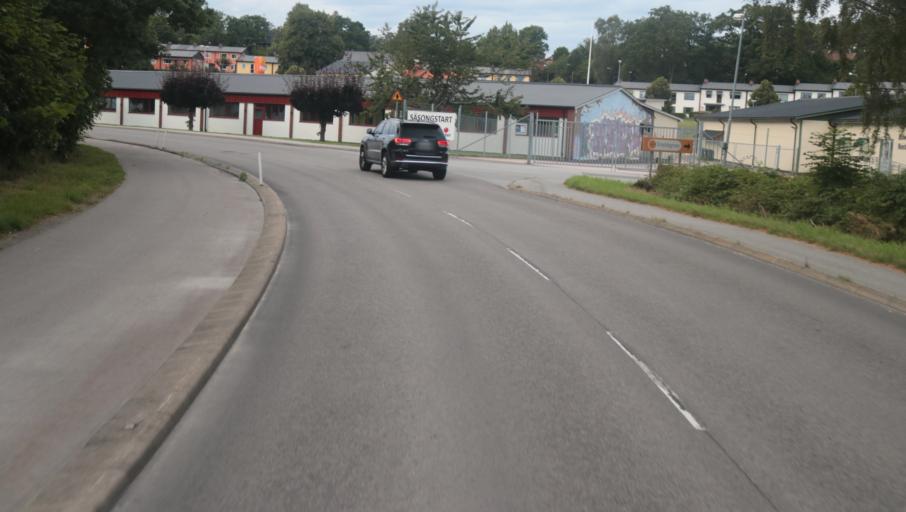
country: SE
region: Blekinge
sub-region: Karlshamns Kommun
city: Karlshamn
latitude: 56.1657
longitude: 14.8834
